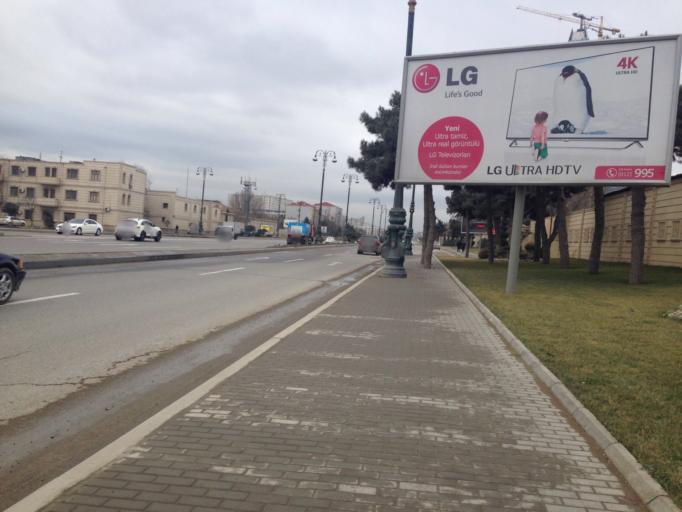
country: AZ
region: Baki
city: Baku
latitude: 40.4079
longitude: 49.8901
